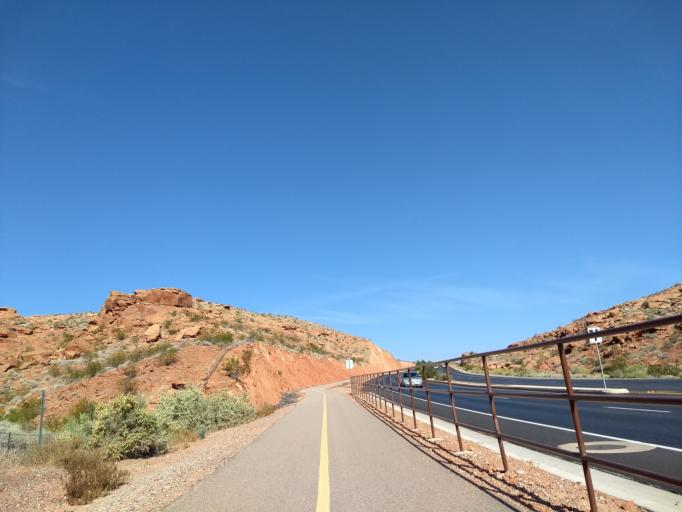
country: US
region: Utah
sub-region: Washington County
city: Saint George
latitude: 37.1188
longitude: -113.5828
